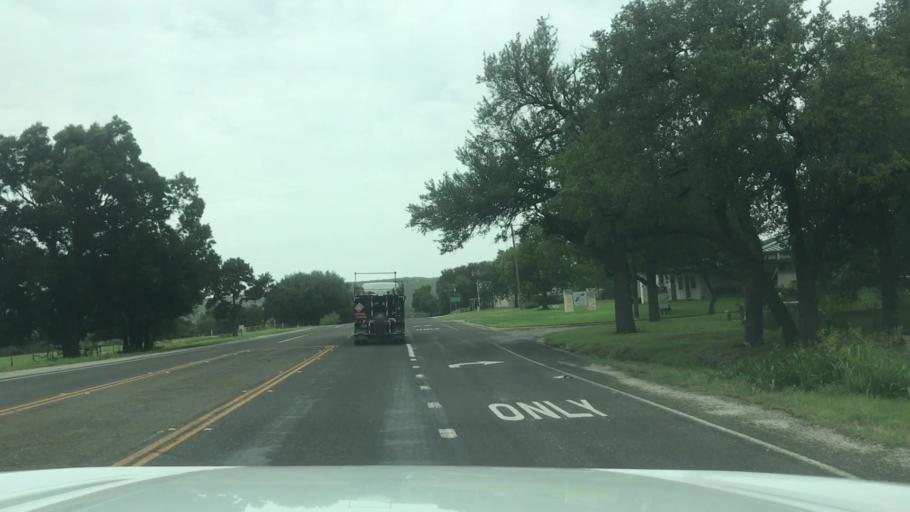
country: US
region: Texas
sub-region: Bosque County
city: Meridian
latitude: 31.9114
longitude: -97.6615
